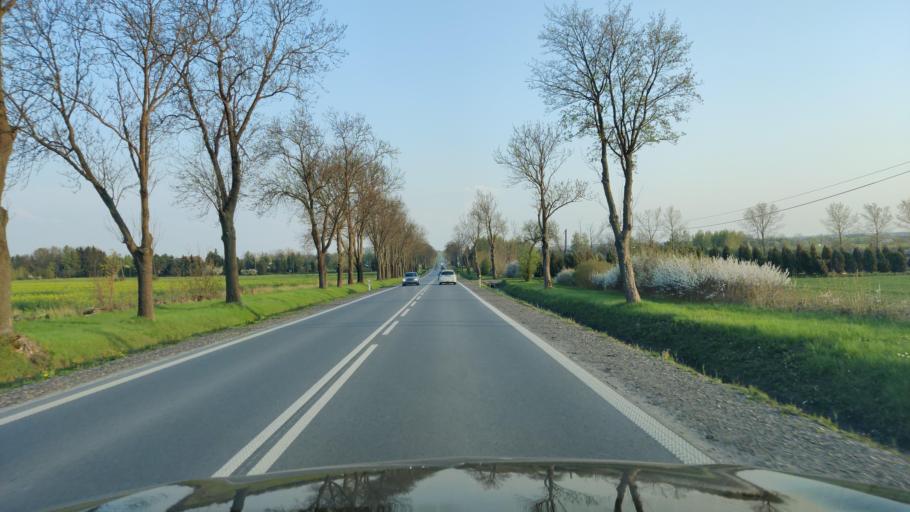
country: PL
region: Masovian Voivodeship
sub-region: Powiat pultuski
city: Pultusk
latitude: 52.6786
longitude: 21.0810
